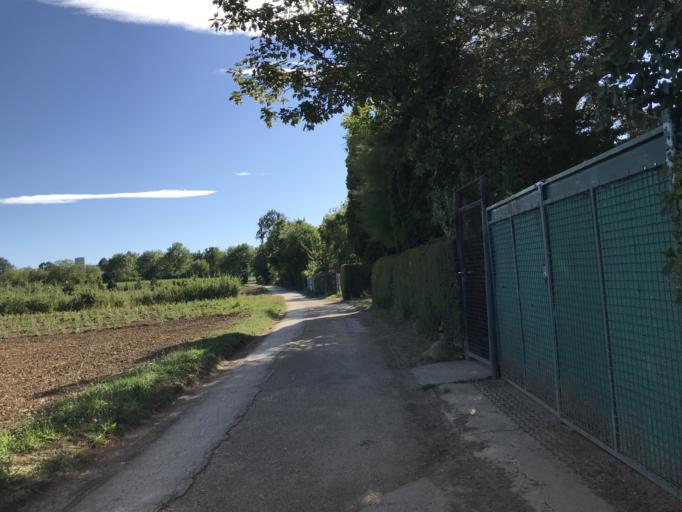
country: DE
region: Baden-Wuerttemberg
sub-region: Regierungsbezirk Stuttgart
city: Leinfelden-Echterdingen
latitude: 48.7356
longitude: 9.1315
